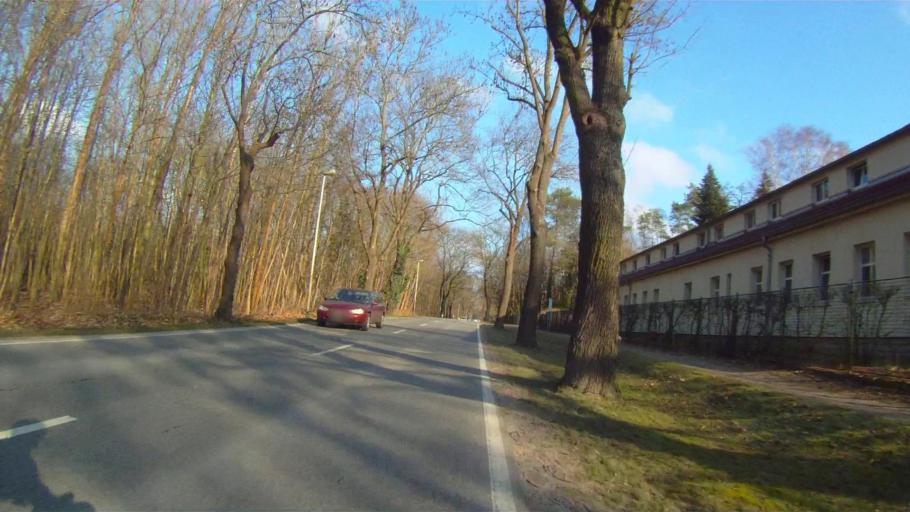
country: DE
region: Brandenburg
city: Woltersdorf
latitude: 52.4569
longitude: 13.7560
